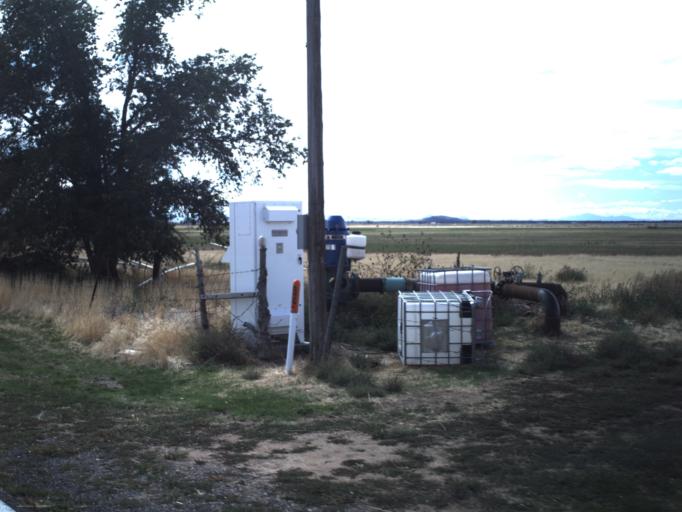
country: US
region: Utah
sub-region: Millard County
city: Fillmore
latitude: 39.0401
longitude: -112.4099
